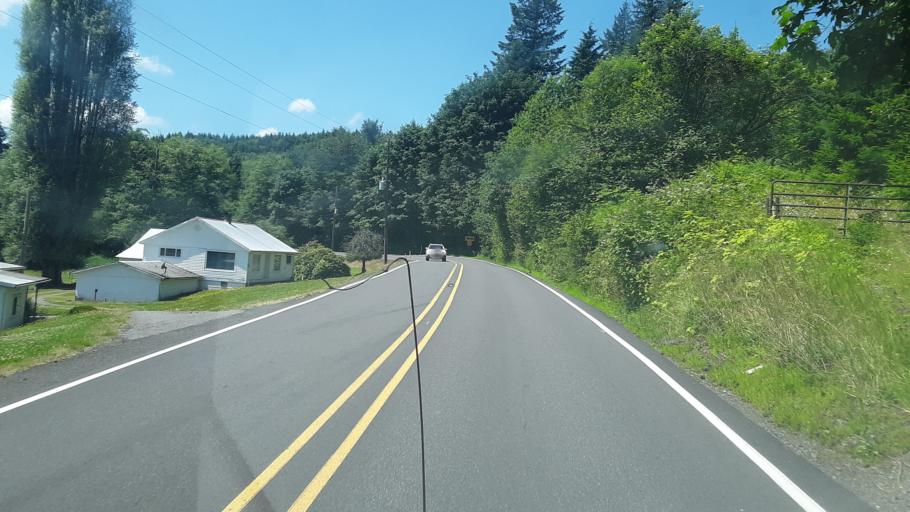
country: US
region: Washington
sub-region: Clark County
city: Amboy
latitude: 45.9458
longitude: -122.3731
